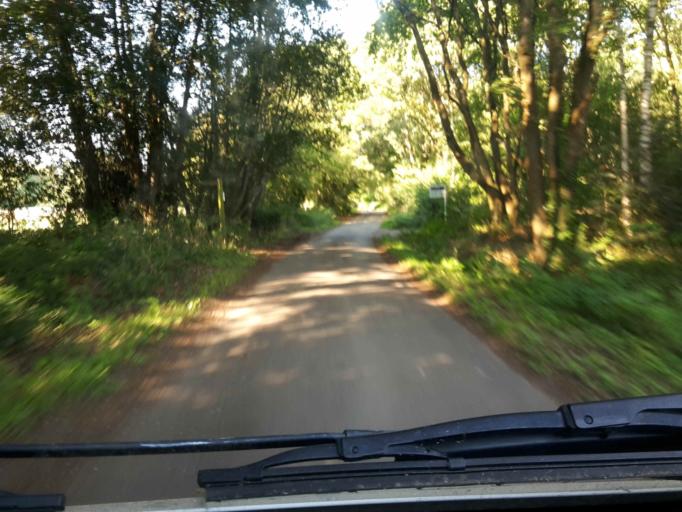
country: GB
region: England
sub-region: Surrey
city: Bramley
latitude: 51.1842
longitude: -0.5356
